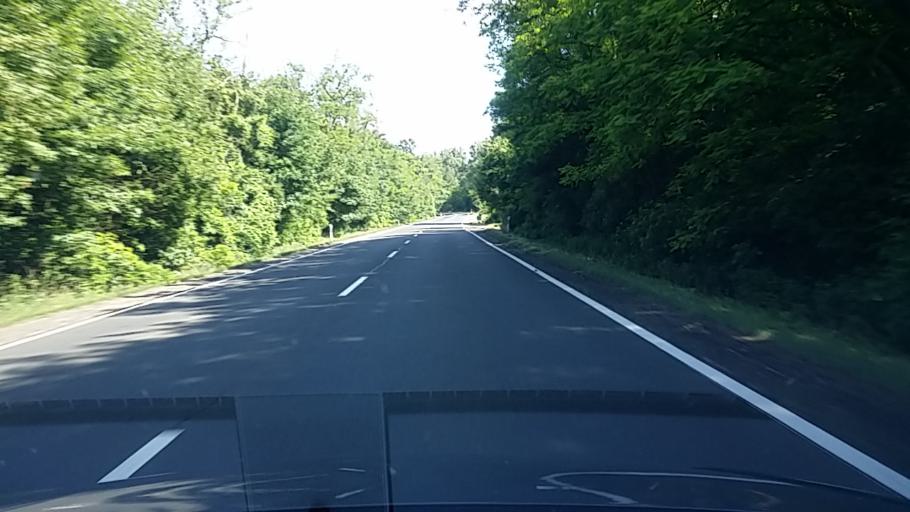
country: HU
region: Nograd
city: Retsag
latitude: 47.9627
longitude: 19.1312
